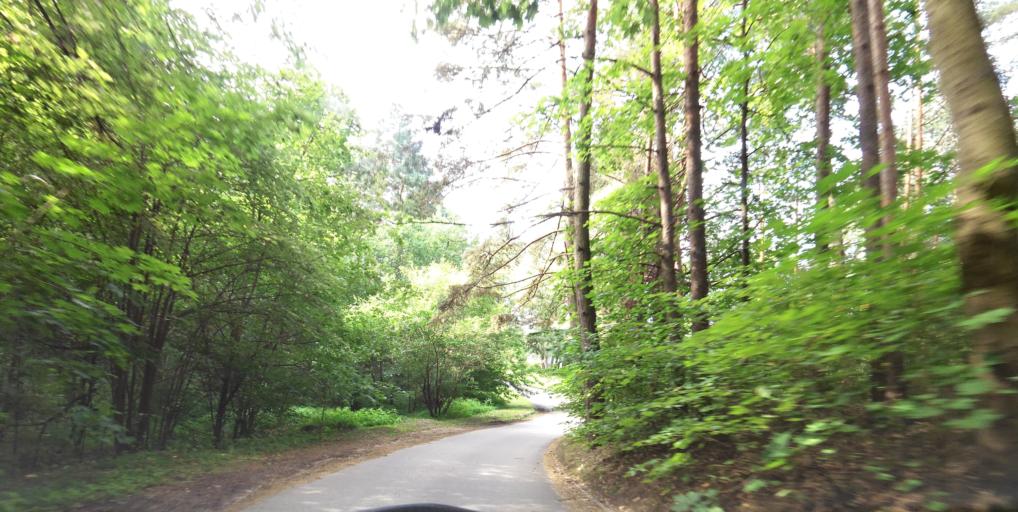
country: LT
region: Vilnius County
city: Seskine
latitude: 54.7300
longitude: 25.2856
